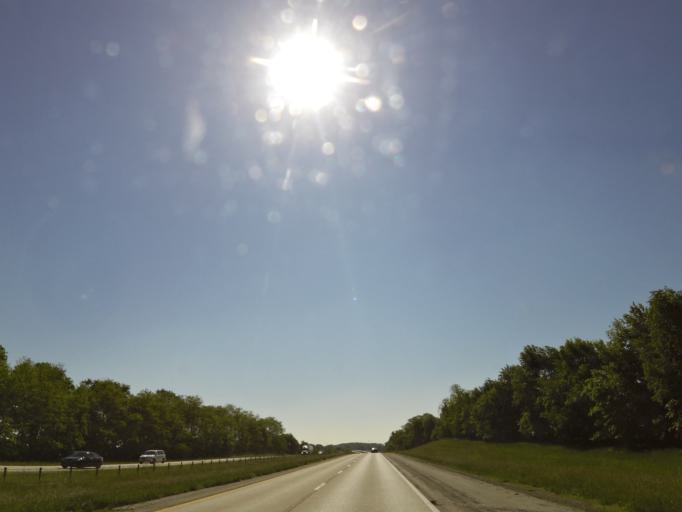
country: US
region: Kentucky
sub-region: Woodford County
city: Midway
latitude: 38.1661
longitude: -84.7525
